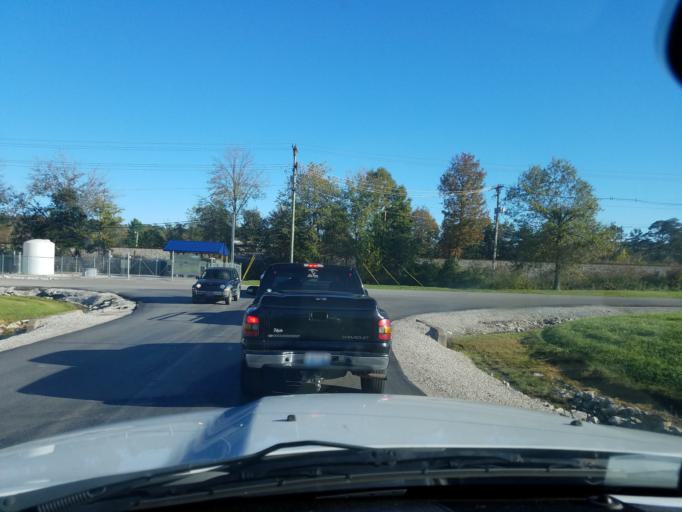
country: US
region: Kentucky
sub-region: Laurel County
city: North Corbin
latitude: 37.0341
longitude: -84.0631
